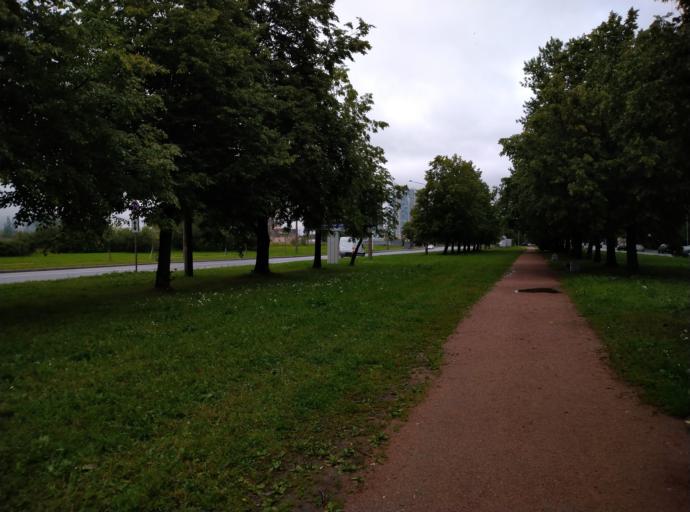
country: RU
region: St.-Petersburg
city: Kupchino
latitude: 59.8465
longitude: 30.3555
